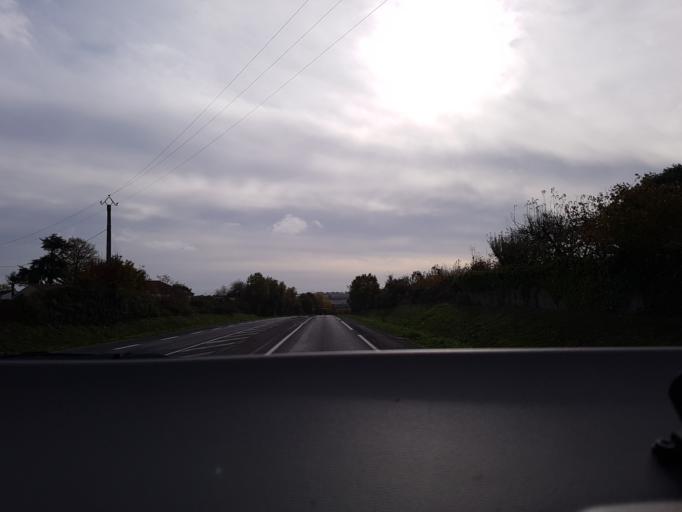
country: FR
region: Pays de la Loire
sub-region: Departement de Maine-et-Loire
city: Beaupreau
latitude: 47.1981
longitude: -0.9740
